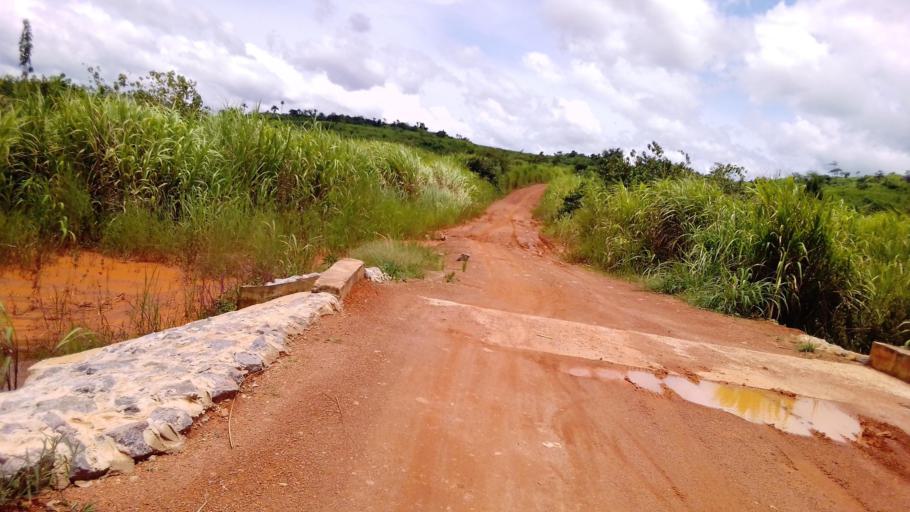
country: SL
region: Eastern Province
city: Koidu
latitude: 8.6789
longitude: -10.9358
